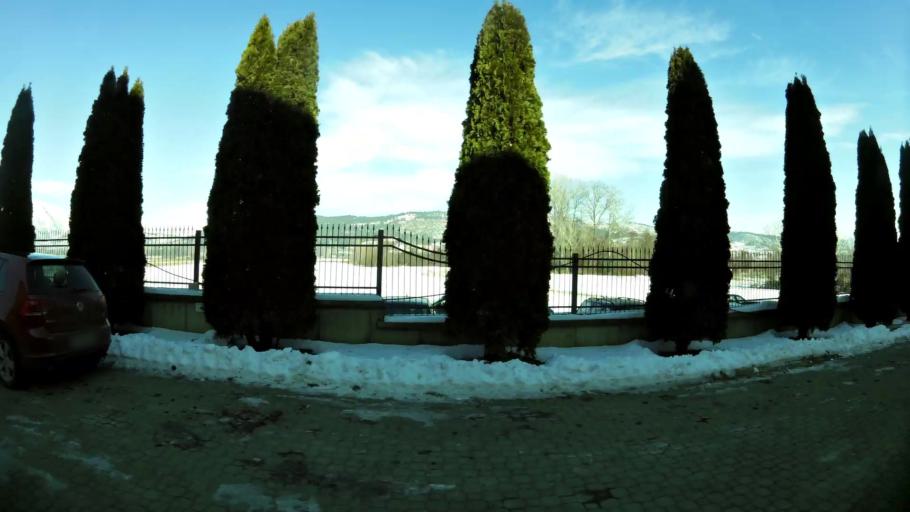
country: MK
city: Ljubin
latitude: 42.0036
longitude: 21.3002
